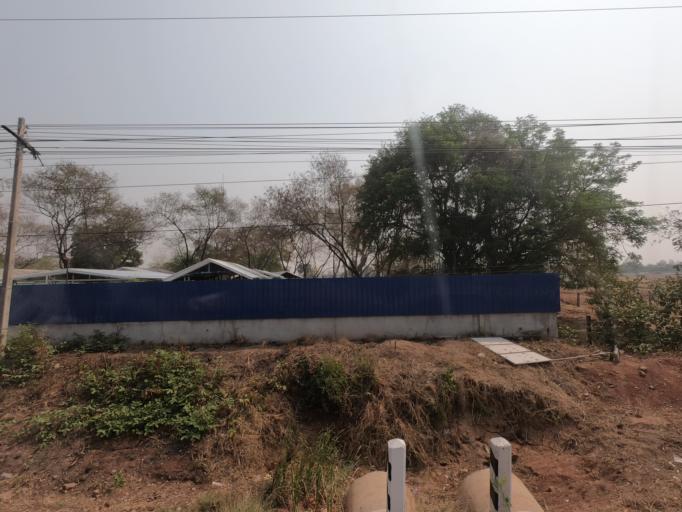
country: TH
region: Nakhon Ratchasima
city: Bua Lai
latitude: 15.6358
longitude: 102.5689
